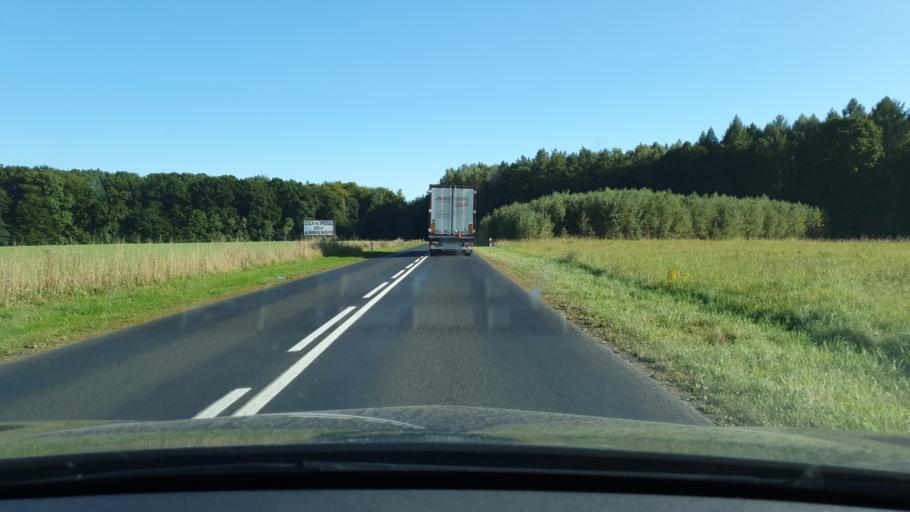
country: PL
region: West Pomeranian Voivodeship
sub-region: Powiat kamienski
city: Golczewo
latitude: 53.8125
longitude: 15.0006
